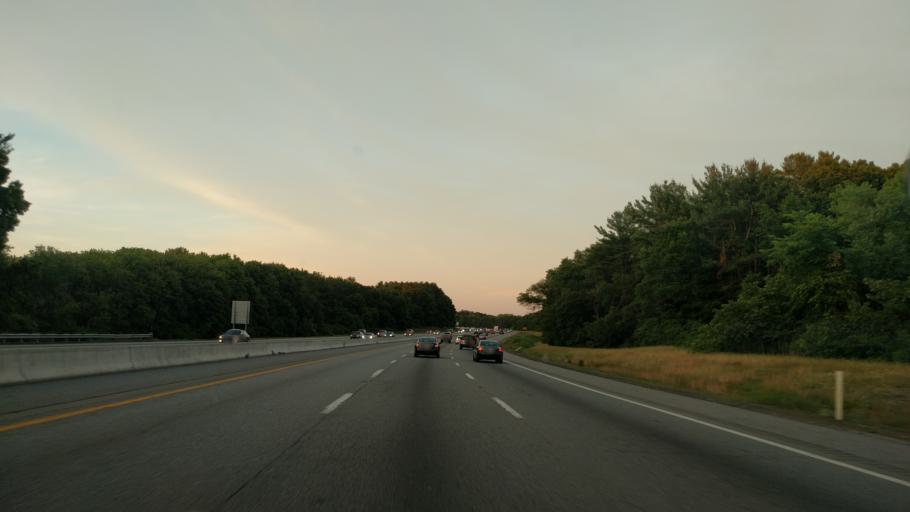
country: US
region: Massachusetts
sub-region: Middlesex County
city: Cochituate
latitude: 42.3164
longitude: -71.3560
